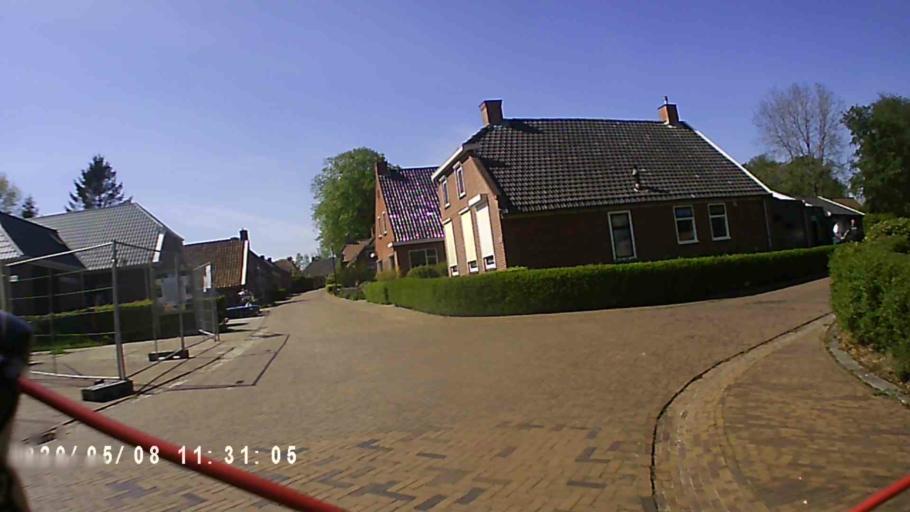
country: NL
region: Groningen
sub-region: Gemeente Bedum
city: Bedum
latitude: 53.3452
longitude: 6.7101
